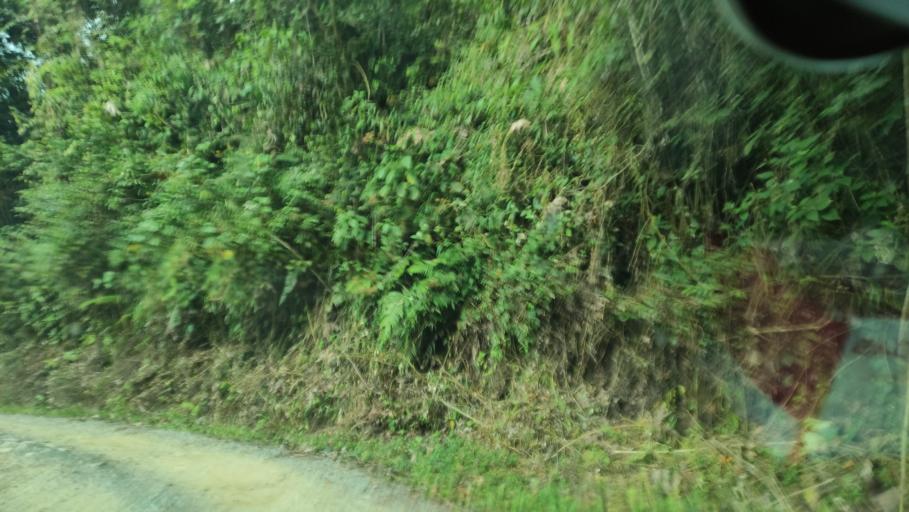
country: CO
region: Valle del Cauca
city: San Pedro
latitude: 3.8780
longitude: -76.1614
